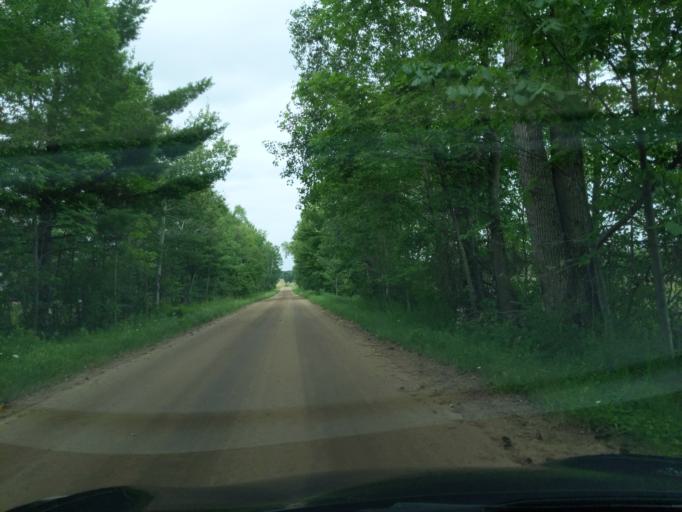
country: US
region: Michigan
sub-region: Clare County
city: Harrison
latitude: 43.9878
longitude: -85.0026
